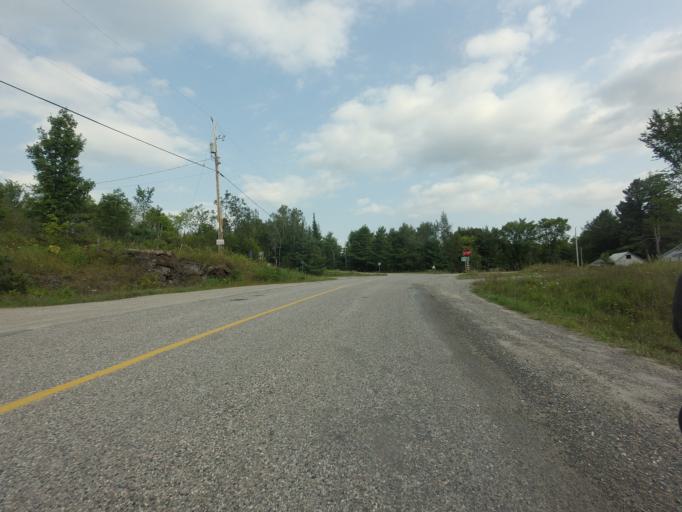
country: CA
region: Ontario
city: Perth
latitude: 44.8724
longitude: -76.7022
